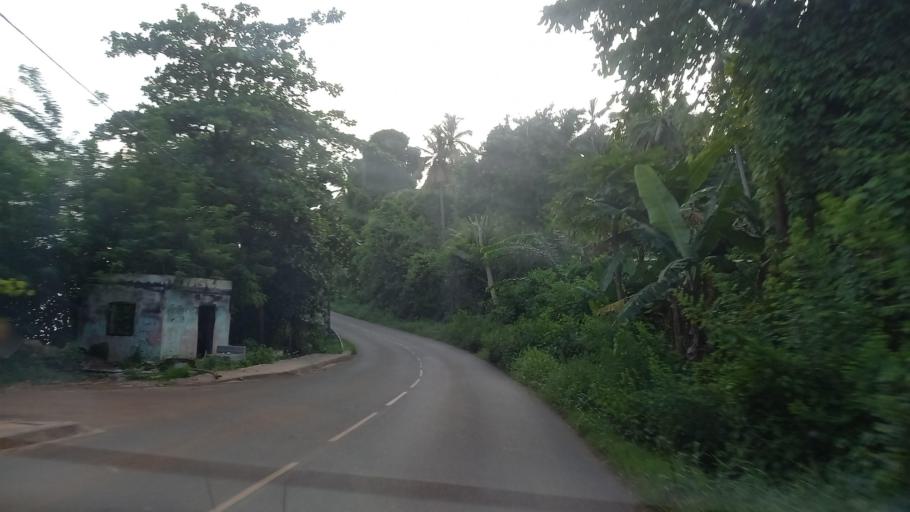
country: YT
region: M'Tsangamouji
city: M'Tsangamouji
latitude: -12.7635
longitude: 45.0810
